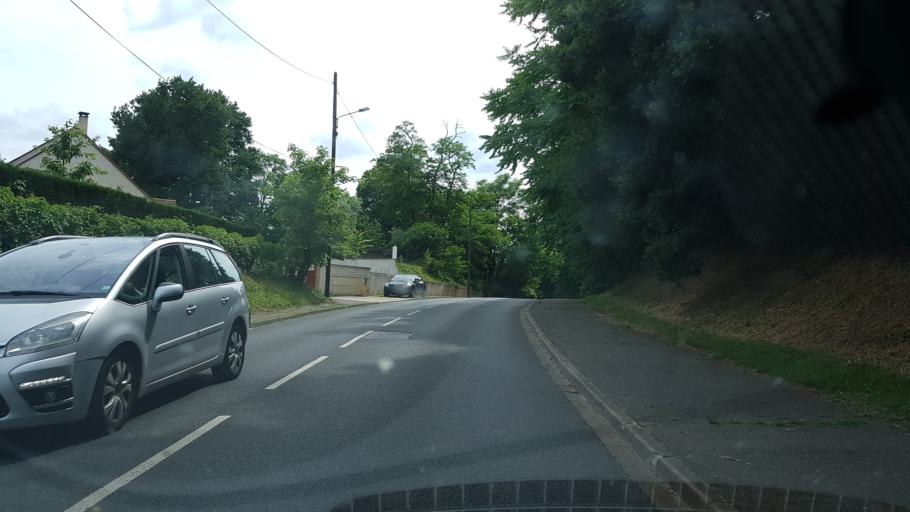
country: FR
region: Ile-de-France
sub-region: Departement des Yvelines
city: Saint-Remy-les-Chevreuse
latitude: 48.7091
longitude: 2.0628
